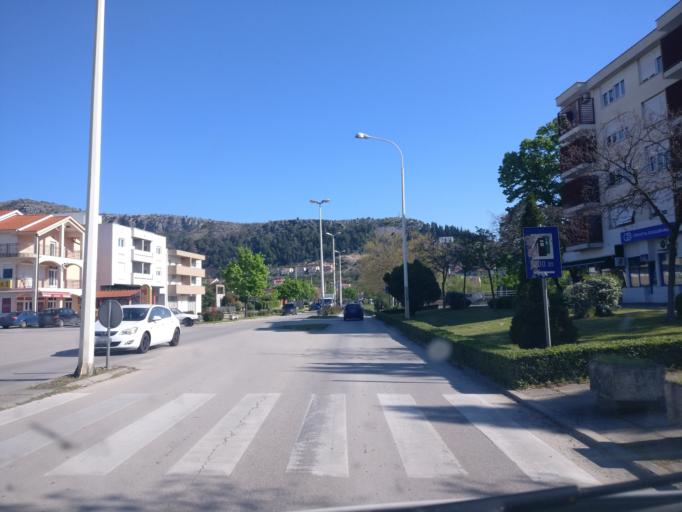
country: BA
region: Federation of Bosnia and Herzegovina
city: Capljina
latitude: 43.1109
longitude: 17.6995
